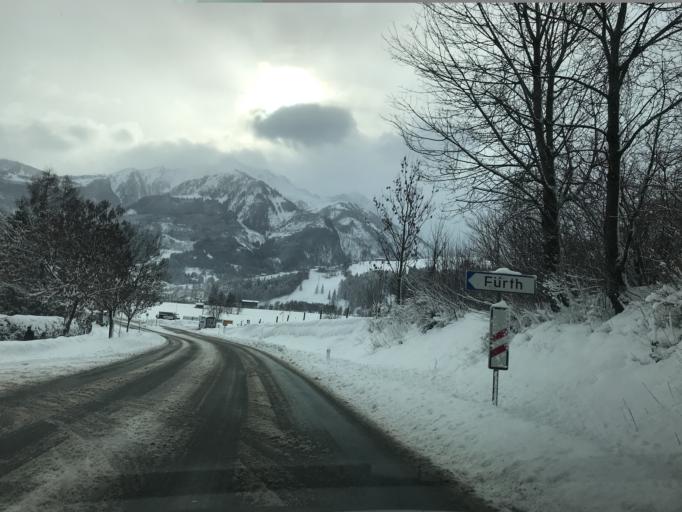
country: AT
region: Salzburg
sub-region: Politischer Bezirk Zell am See
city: Kaprun
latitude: 47.2894
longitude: 12.7455
